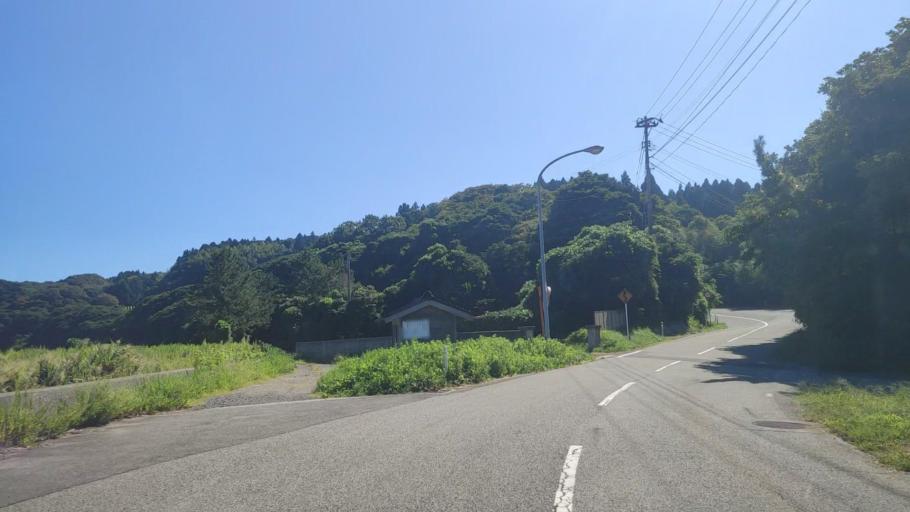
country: JP
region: Ishikawa
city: Nanao
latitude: 37.5221
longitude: 137.3266
